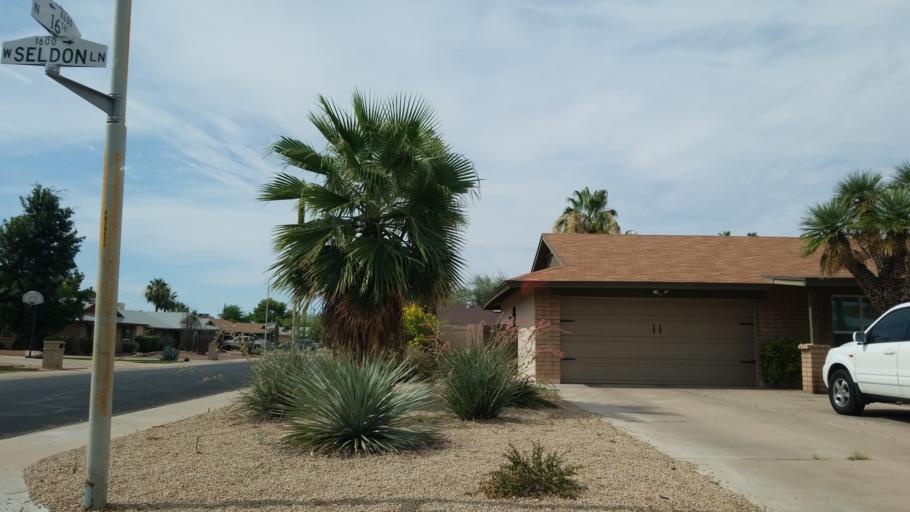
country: US
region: Arizona
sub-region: Maricopa County
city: Glendale
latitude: 33.5627
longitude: -112.0940
